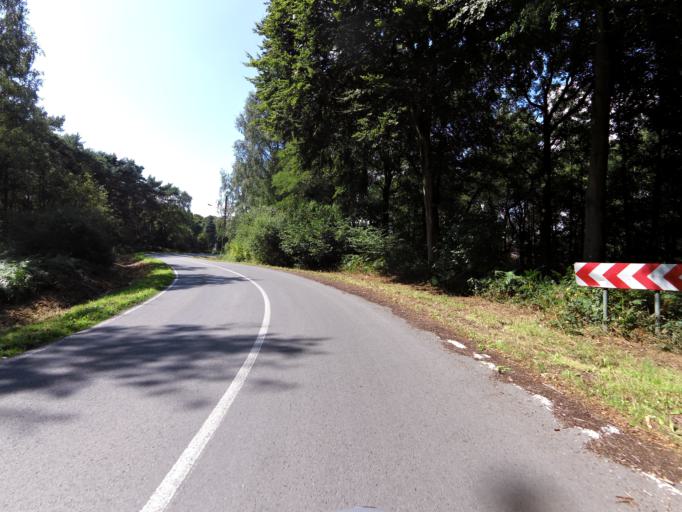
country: BE
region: Wallonia
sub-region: Province du Hainaut
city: Saint-Ghislain
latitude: 50.4925
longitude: 3.8086
